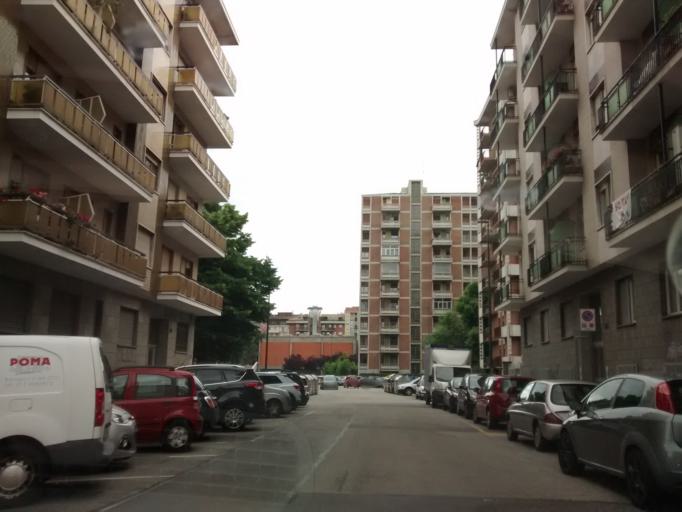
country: IT
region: Piedmont
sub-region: Provincia di Torino
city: Lesna
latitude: 45.0420
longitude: 7.6415
